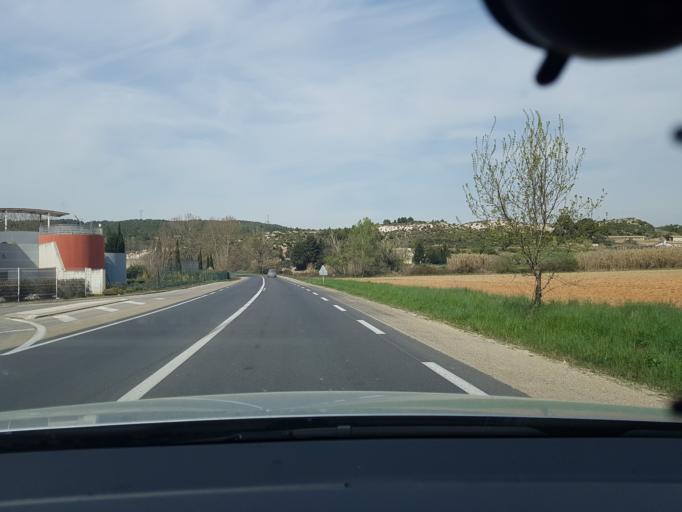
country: FR
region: Provence-Alpes-Cote d'Azur
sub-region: Departement des Bouches-du-Rhone
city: Gardanne
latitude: 43.4687
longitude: 5.4612
